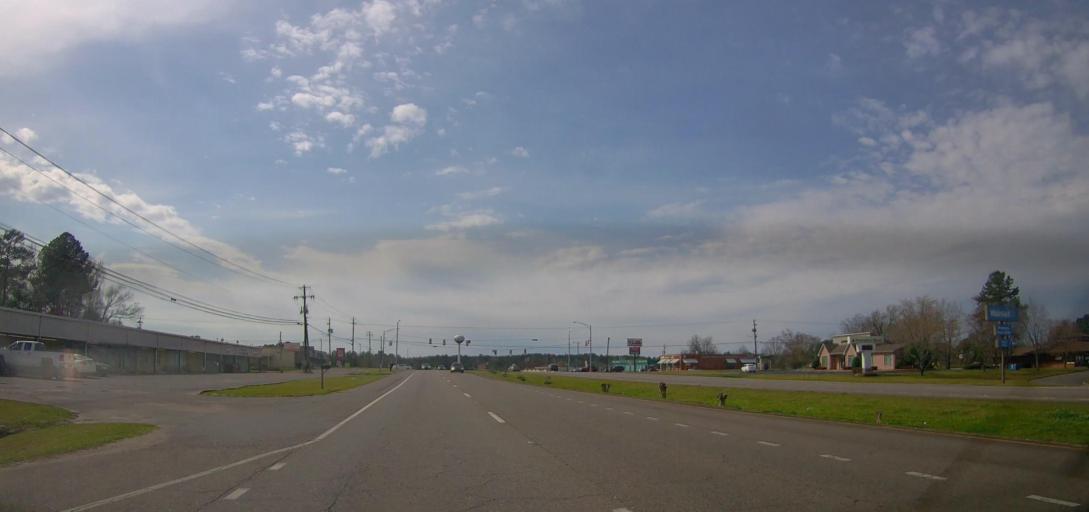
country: US
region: Alabama
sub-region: Walker County
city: Sumiton
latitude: 33.7436
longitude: -87.0436
